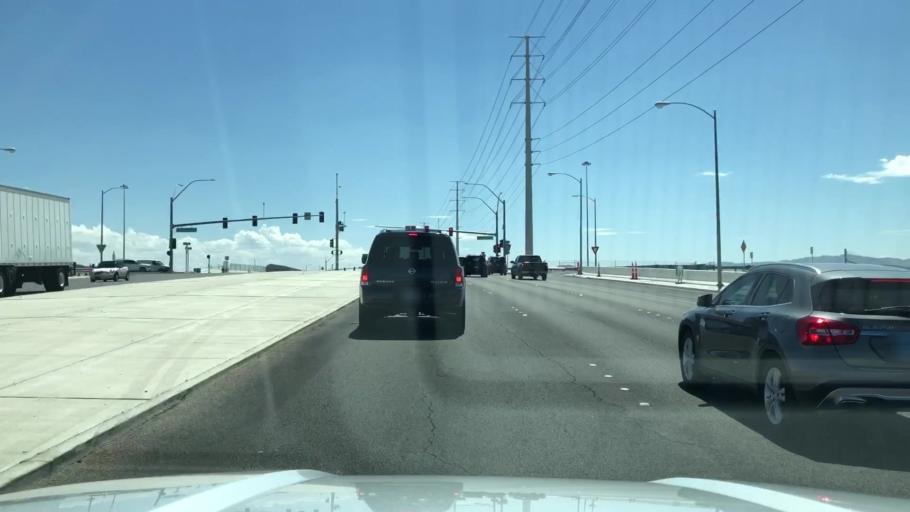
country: US
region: Nevada
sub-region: Clark County
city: Spring Valley
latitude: 36.0683
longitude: -115.2795
